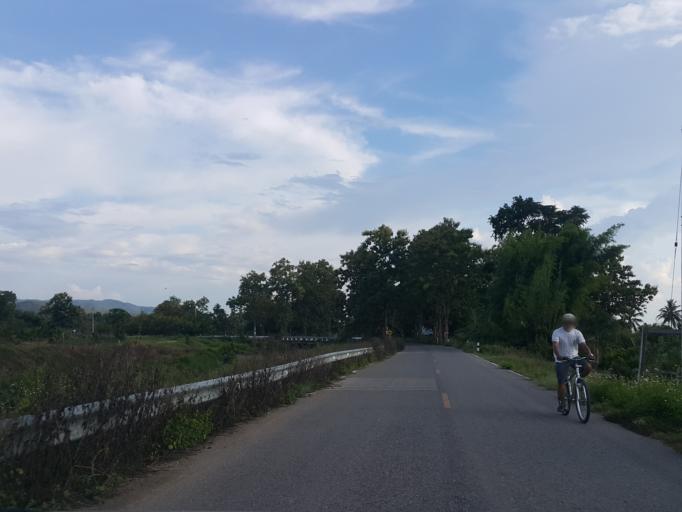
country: TH
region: Chiang Mai
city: Mae Taeng
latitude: 19.0460
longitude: 98.9764
